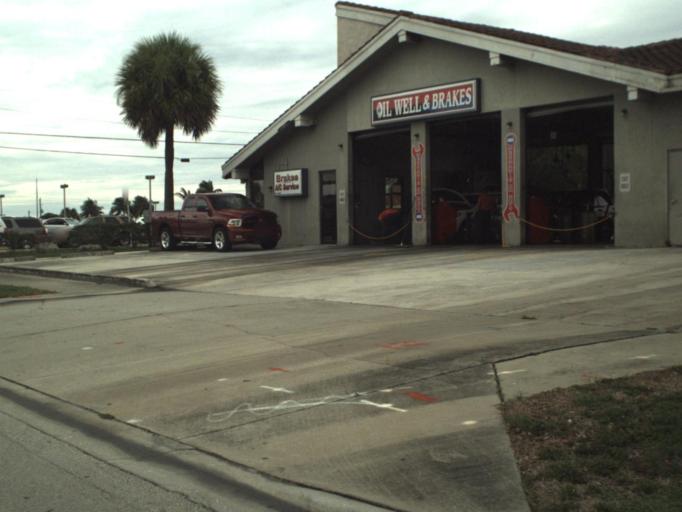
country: US
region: Florida
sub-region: Palm Beach County
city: Lake Clarke Shores
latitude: 26.6759
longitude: -80.0633
